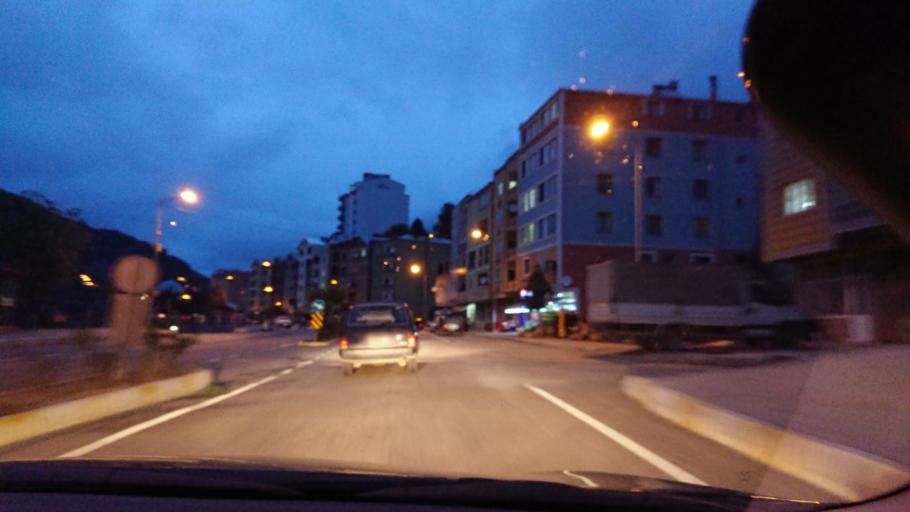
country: TR
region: Gumushane
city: Kurtun
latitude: 40.6678
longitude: 39.1416
